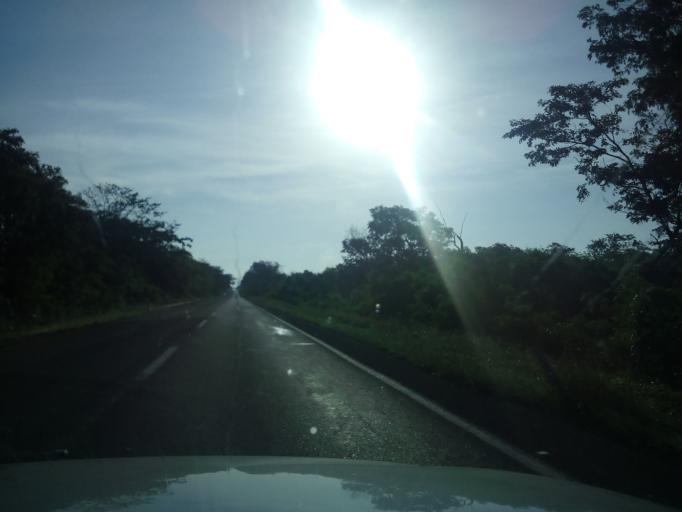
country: MX
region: Yucatan
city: Chichen-Itza
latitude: 20.7111
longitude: -88.4800
